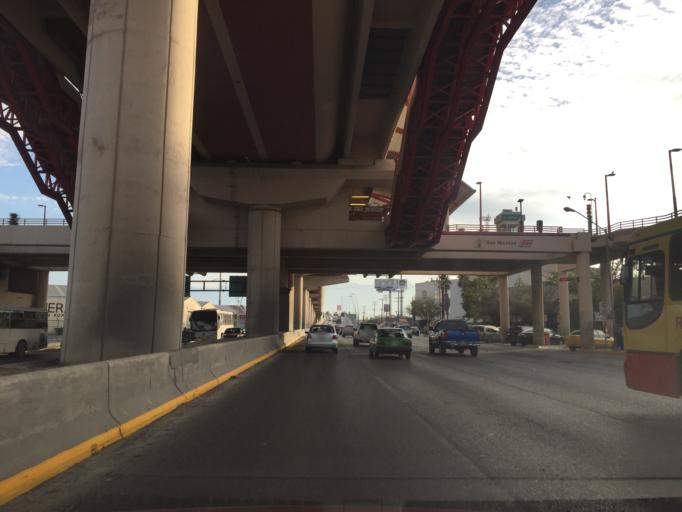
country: MX
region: Nuevo Leon
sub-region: San Nicolas de los Garza
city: San Nicolas de los Garza
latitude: 25.7531
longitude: -100.2979
